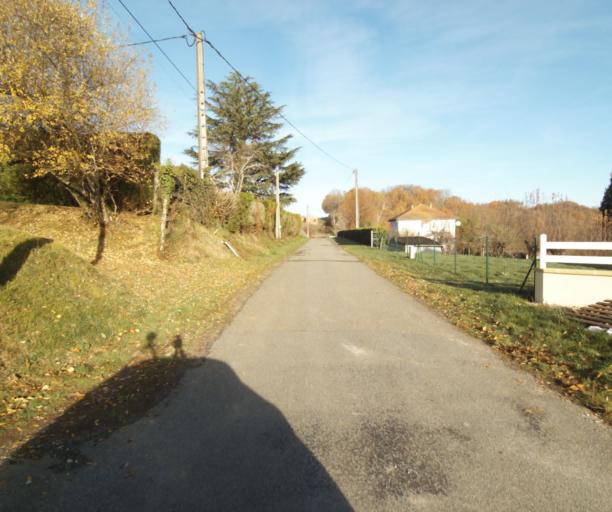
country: FR
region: Limousin
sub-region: Departement de la Correze
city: Laguenne
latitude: 45.2574
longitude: 1.7991
